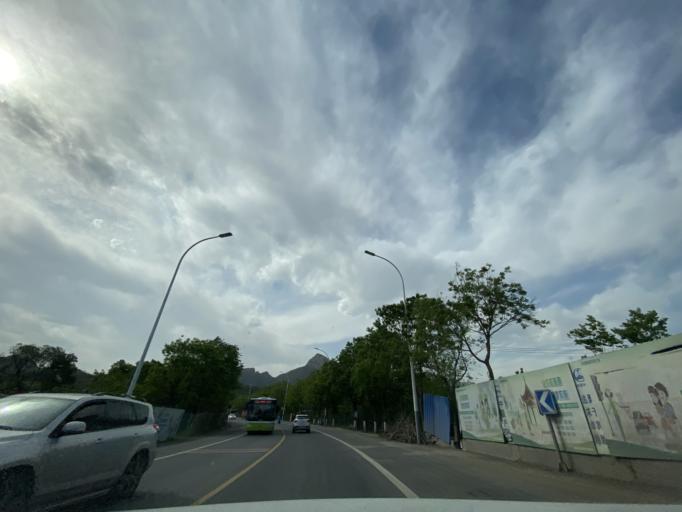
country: CN
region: Beijing
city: Junzhuang
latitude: 39.9902
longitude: 116.0803
